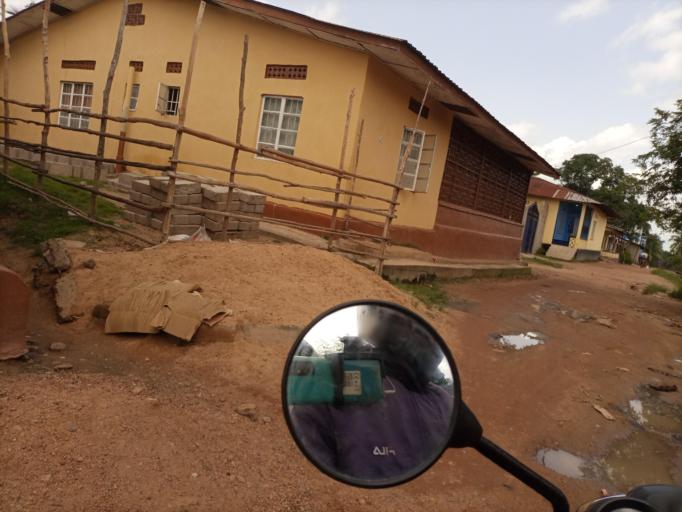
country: SL
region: Southern Province
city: Bo
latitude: 7.9505
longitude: -11.7344
